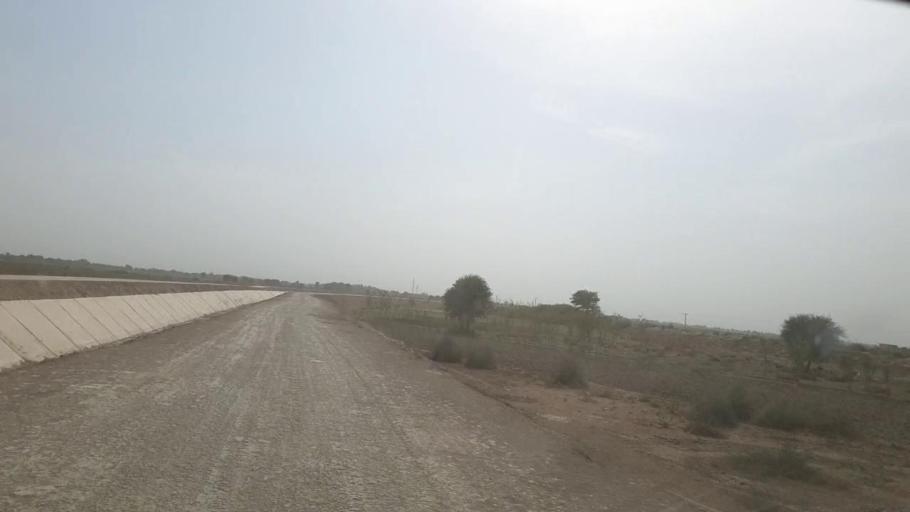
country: PK
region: Sindh
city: Nabisar
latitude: 25.0548
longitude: 69.5330
